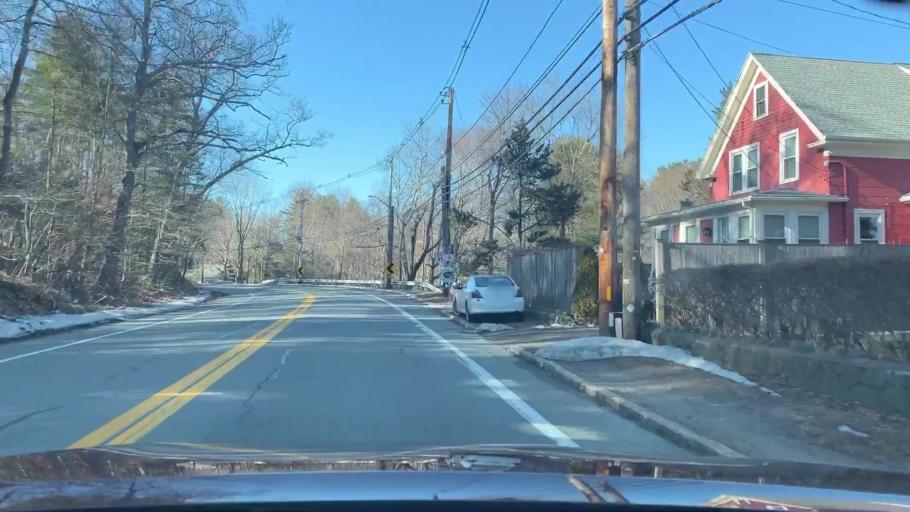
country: US
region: Massachusetts
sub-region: Essex County
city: Gloucester
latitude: 42.6151
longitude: -70.6951
